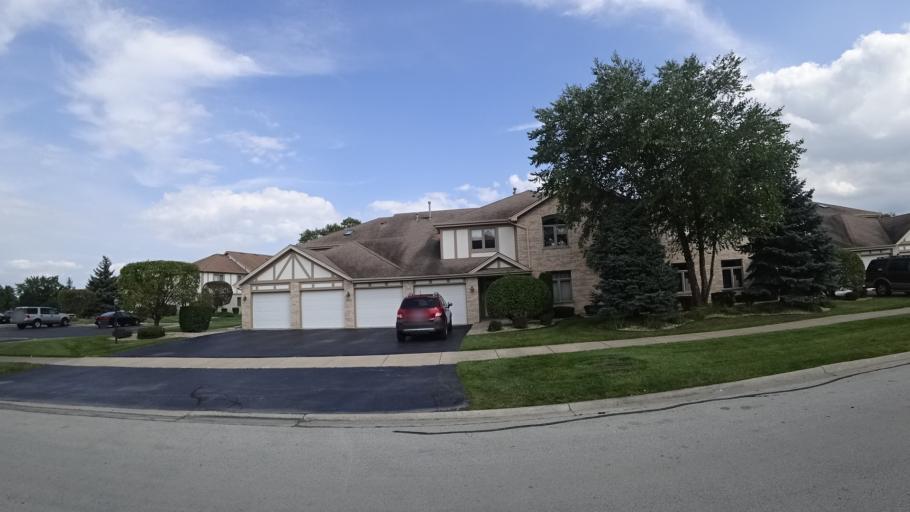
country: US
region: Illinois
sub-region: Cook County
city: Tinley Park
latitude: 41.5544
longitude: -87.7743
